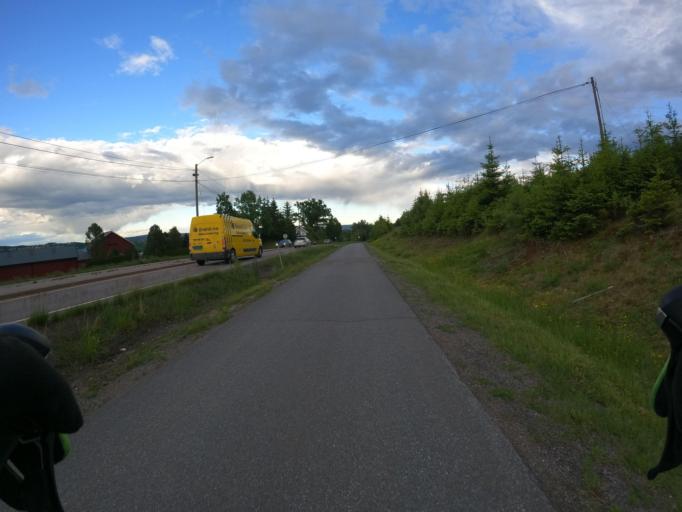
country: NO
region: Akershus
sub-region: Lorenskog
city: Kjenn
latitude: 59.9834
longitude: 10.9621
